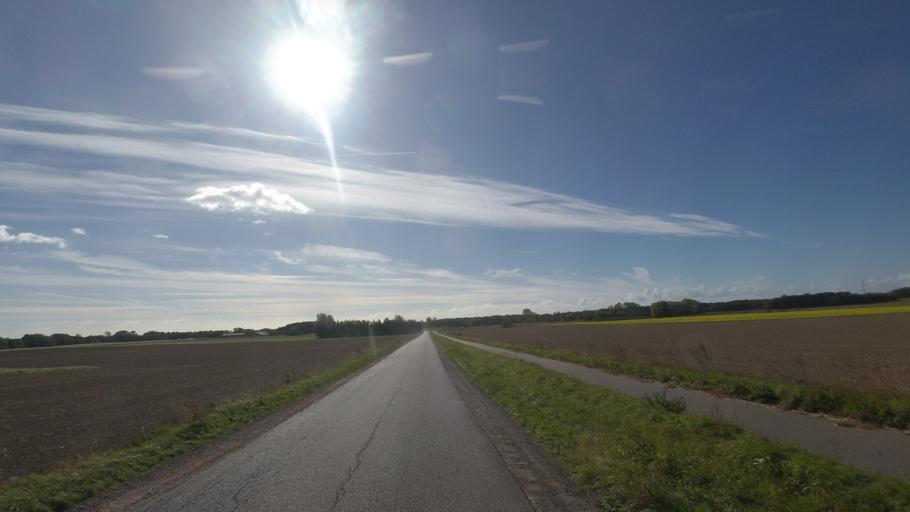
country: DK
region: Capital Region
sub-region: Bornholm Kommune
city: Akirkeby
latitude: 55.0174
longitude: 14.9924
